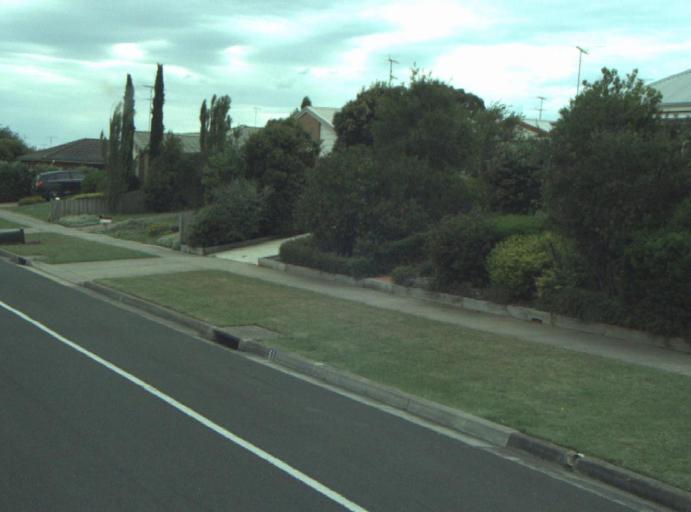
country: AU
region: Victoria
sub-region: Greater Geelong
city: Leopold
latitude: -38.1836
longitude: 144.4611
